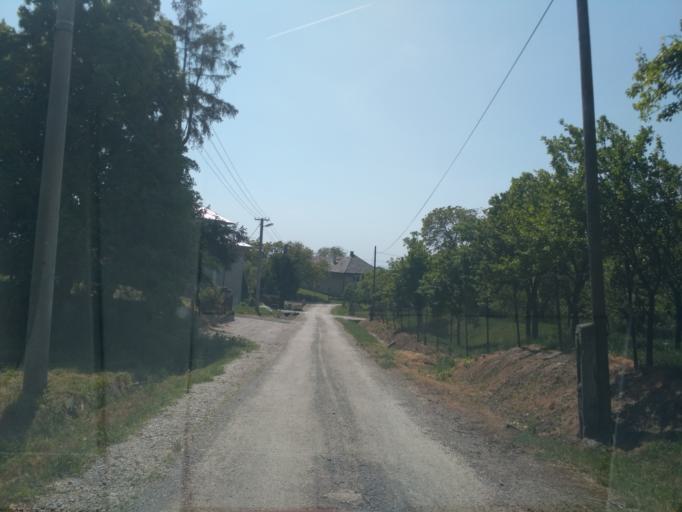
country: SK
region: Kosicky
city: Kosice
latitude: 48.8290
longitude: 21.4504
